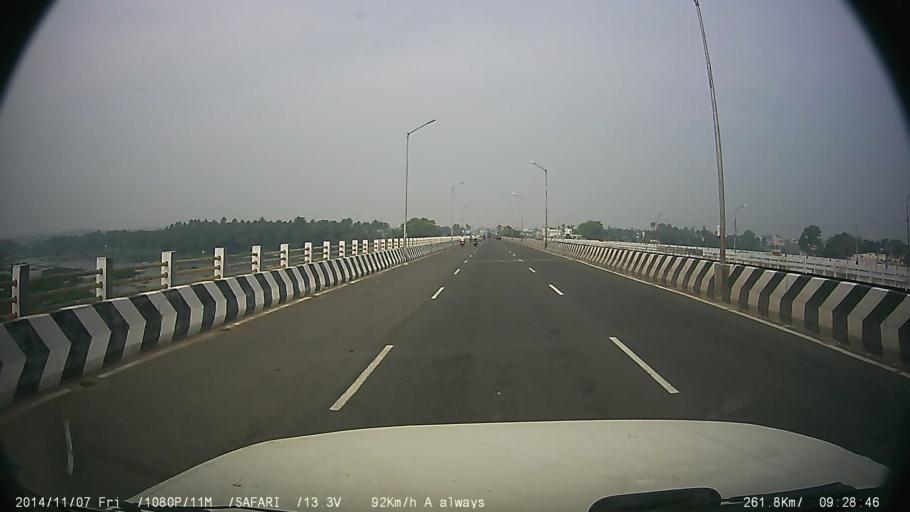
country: IN
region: Tamil Nadu
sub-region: Erode
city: Bhavani
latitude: 11.4315
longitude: 77.6859
